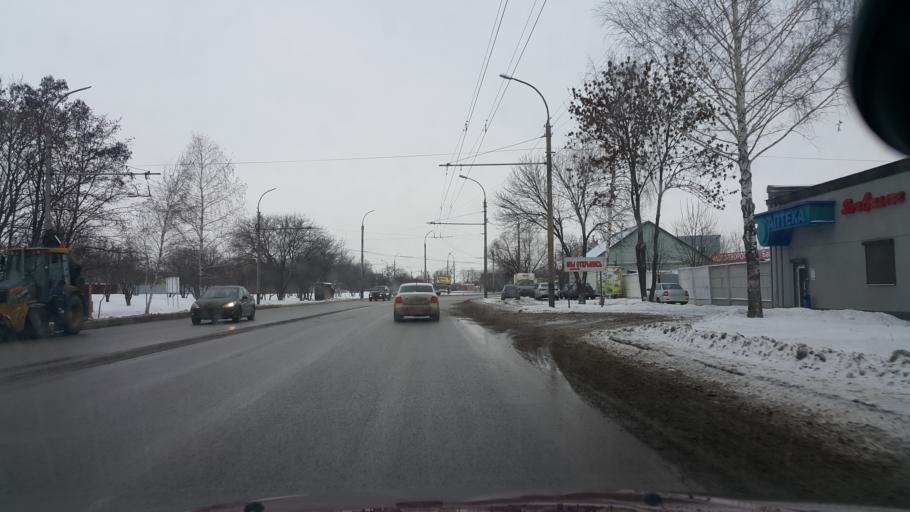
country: RU
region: Tambov
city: Tambov
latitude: 52.7350
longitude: 41.3924
